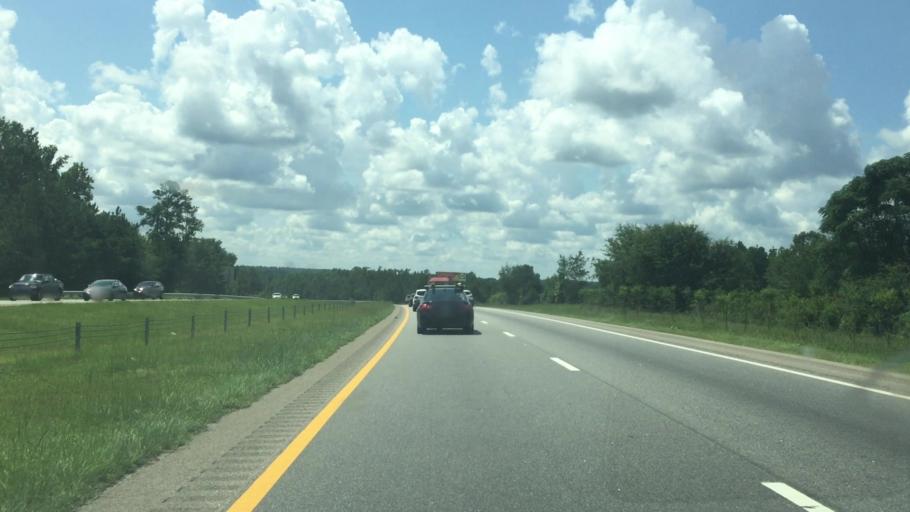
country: US
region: North Carolina
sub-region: Richmond County
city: Cordova
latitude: 34.8957
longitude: -79.7911
